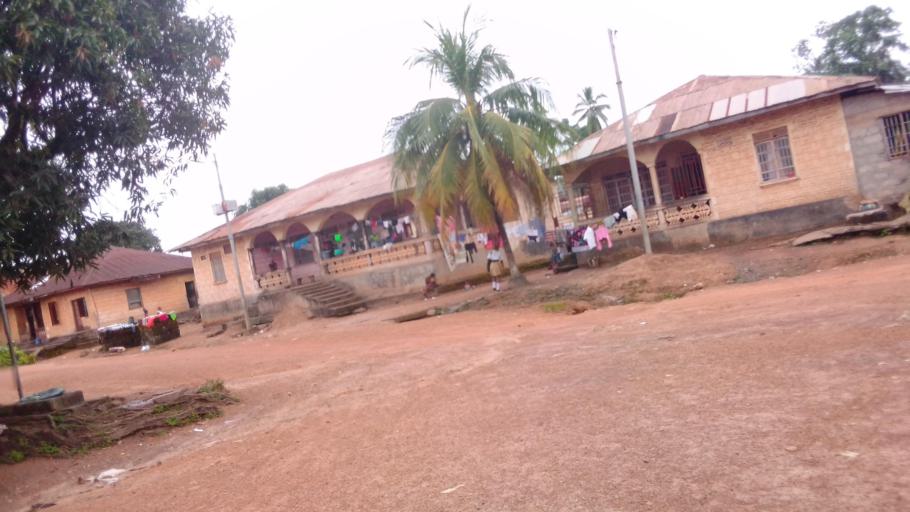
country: SL
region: Northern Province
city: Makeni
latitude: 8.8823
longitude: -12.0425
